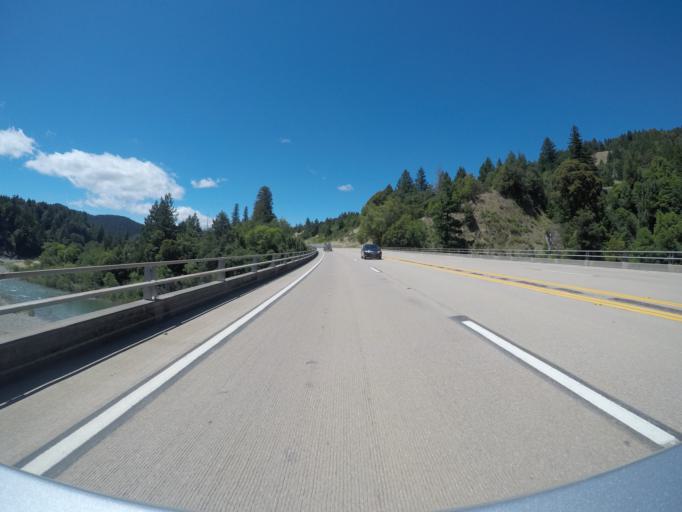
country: US
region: California
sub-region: Humboldt County
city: Redway
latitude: 39.9582
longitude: -123.7816
